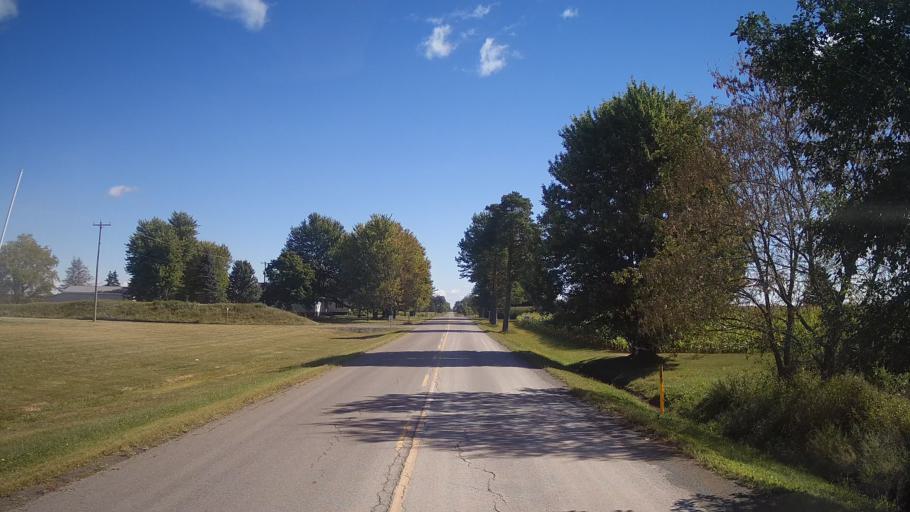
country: CA
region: Ontario
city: Prescott
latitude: 44.9142
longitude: -75.3696
